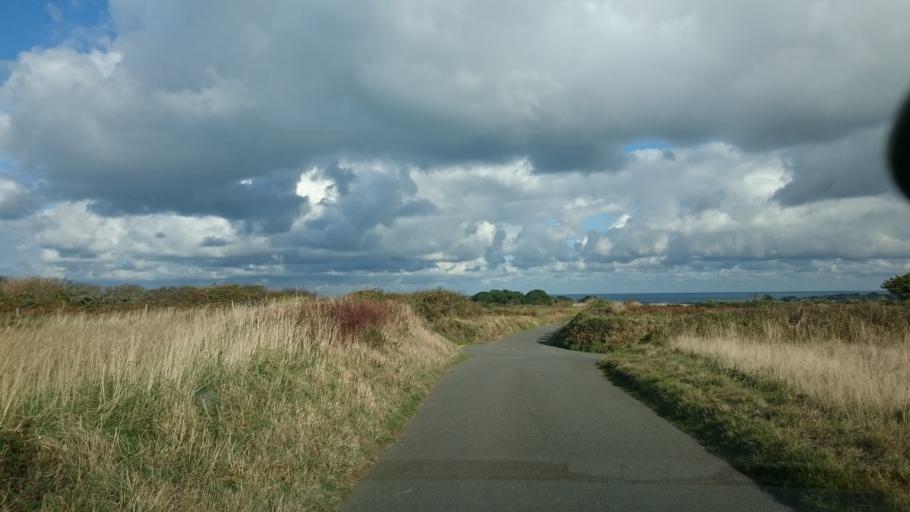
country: GG
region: St Peter Port
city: Saint Peter Port
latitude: 49.4299
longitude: -2.6681
